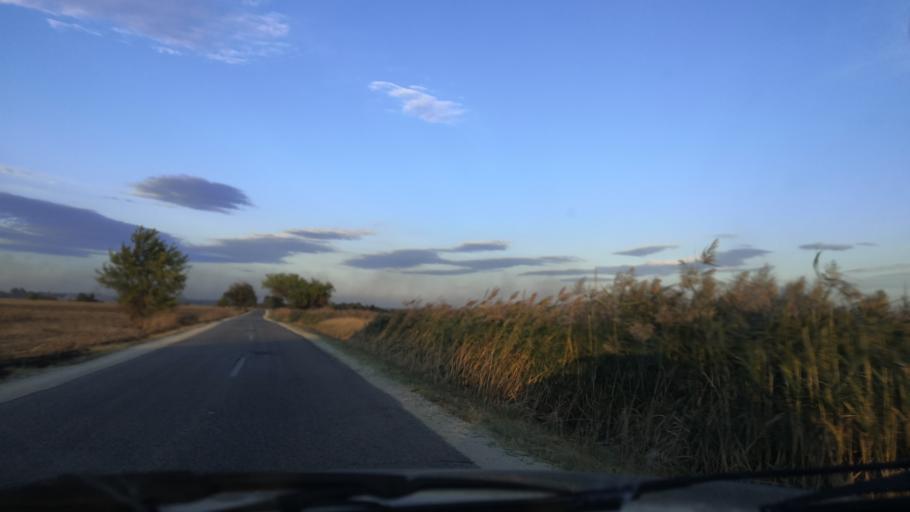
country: RS
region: Central Serbia
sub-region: Borski Okrug
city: Negotin
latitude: 44.2457
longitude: 22.5765
